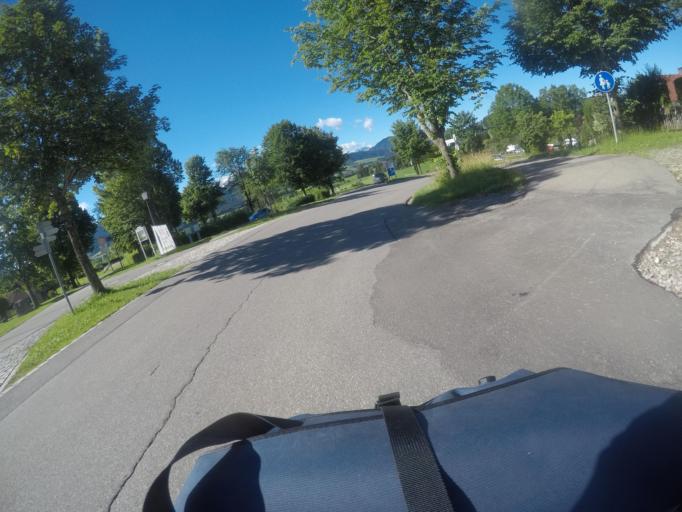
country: DE
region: Bavaria
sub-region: Swabia
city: Oy-Mittelberg
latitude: 47.6412
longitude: 10.4544
